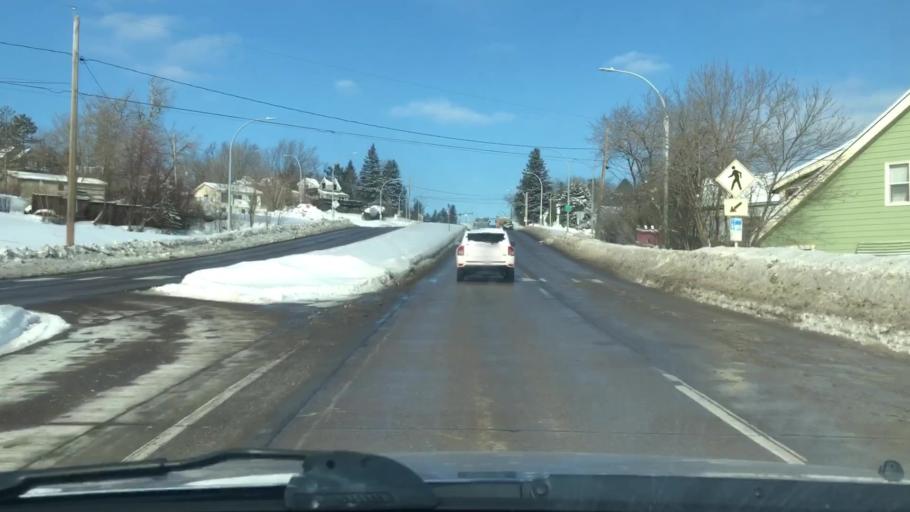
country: US
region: Minnesota
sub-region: Saint Louis County
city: Duluth
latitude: 46.7926
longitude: -92.1070
